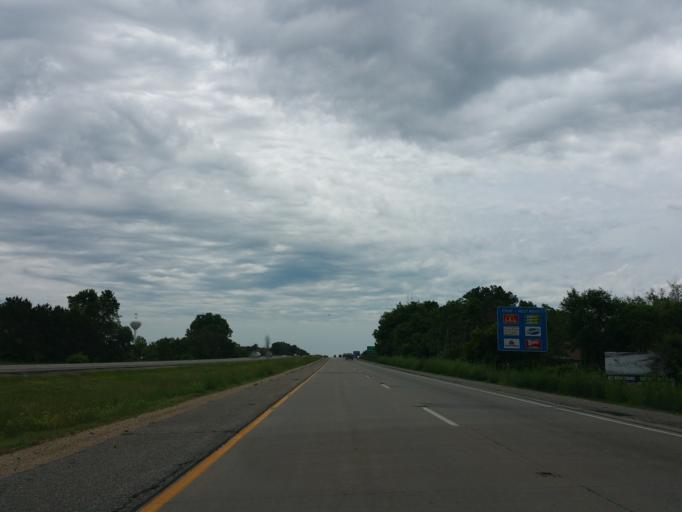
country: US
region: Wisconsin
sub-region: Juneau County
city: Mauston
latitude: 43.8067
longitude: -90.0669
